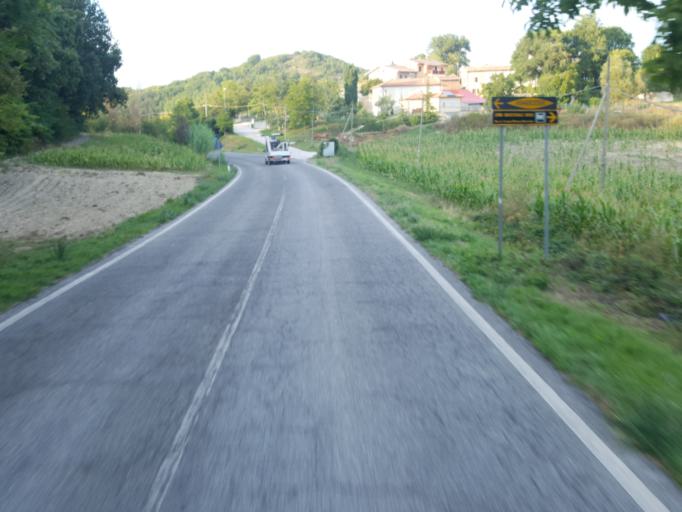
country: IT
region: The Marches
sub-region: Provincia di Ancona
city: Fabriano
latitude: 43.3473
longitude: 12.8298
